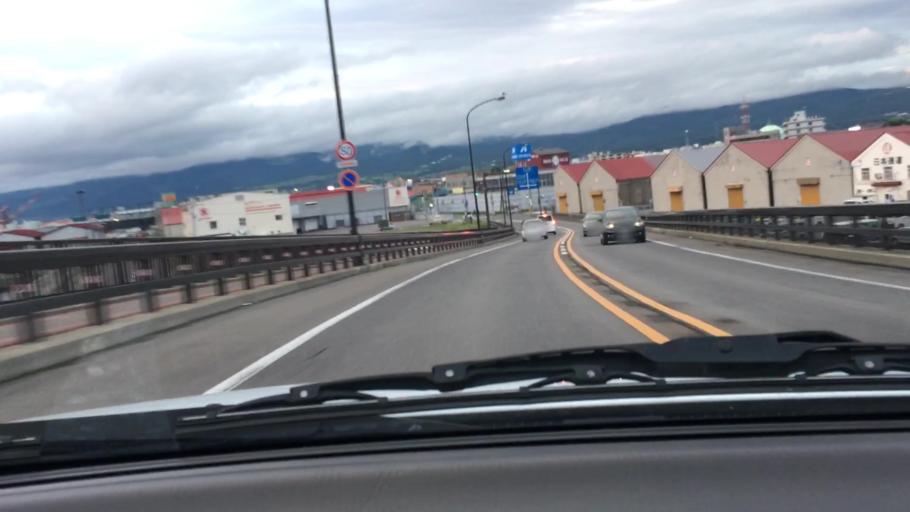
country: JP
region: Hokkaido
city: Hakodate
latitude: 41.7849
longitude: 140.7272
